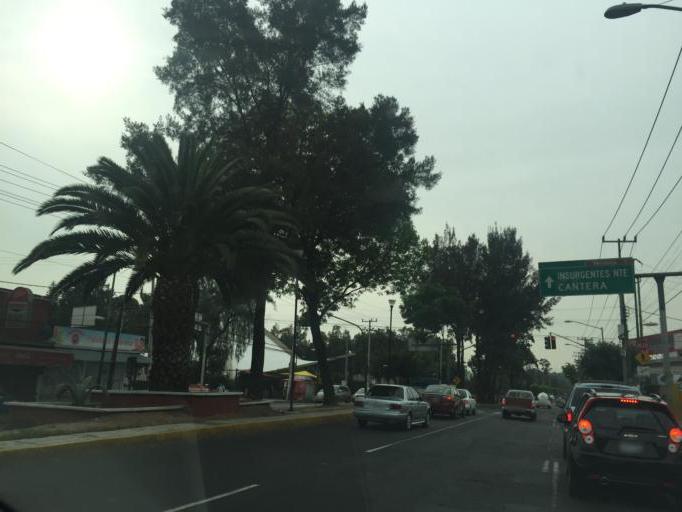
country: MX
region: Mexico
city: Colonia Lindavista
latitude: 19.4991
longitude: -99.1249
